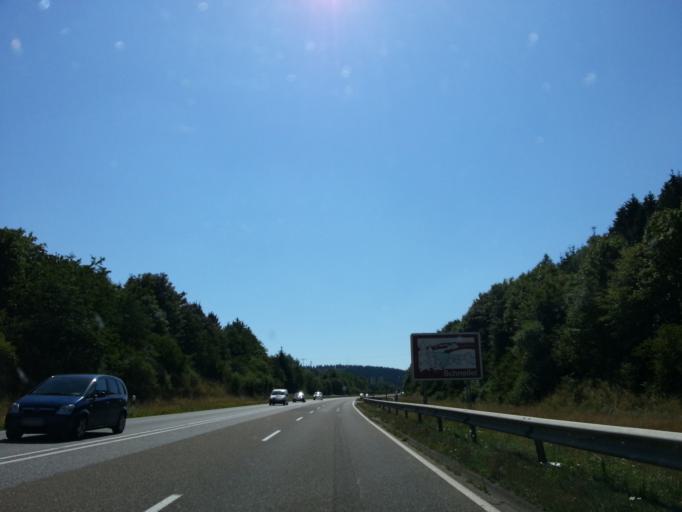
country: DE
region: Rheinland-Pfalz
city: Grosslangenfeld
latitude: 50.2163
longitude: 6.2351
